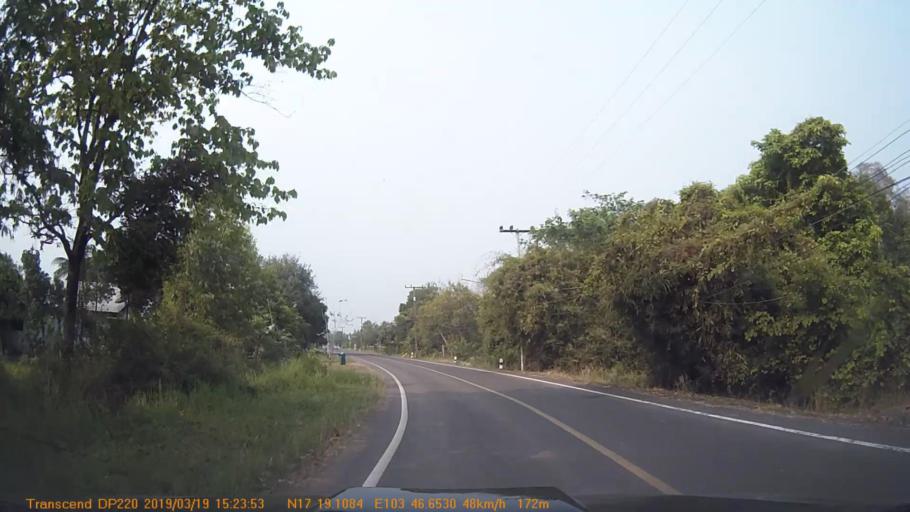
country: TH
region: Sakon Nakhon
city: Phanna Nikhom
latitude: 17.3185
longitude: 103.7776
